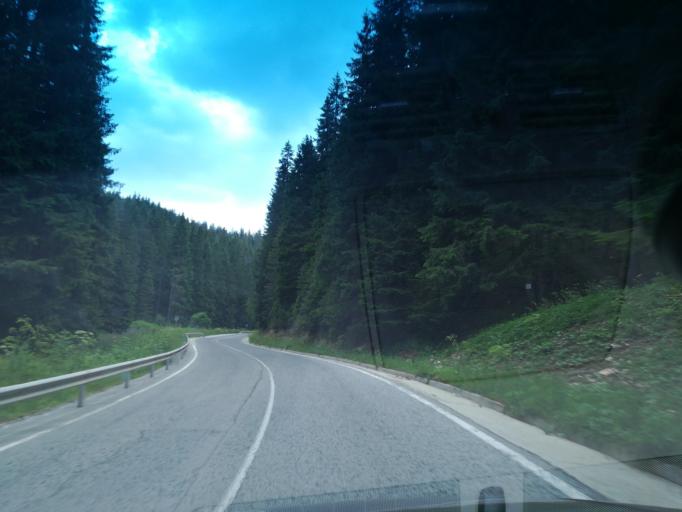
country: BG
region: Smolyan
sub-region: Obshtina Chepelare
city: Chepelare
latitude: 41.6667
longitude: 24.7141
